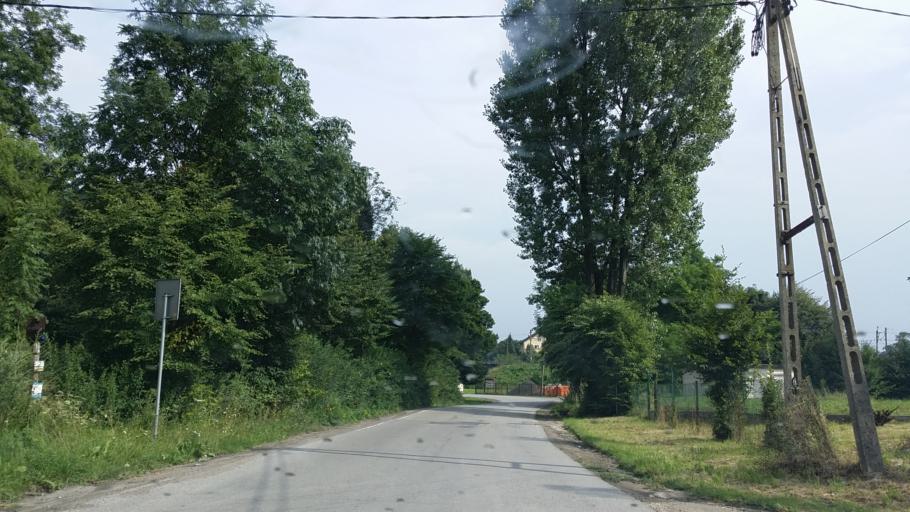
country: PL
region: Lesser Poland Voivodeship
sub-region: Powiat wadowicki
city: Spytkowice
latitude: 50.0031
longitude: 19.5129
